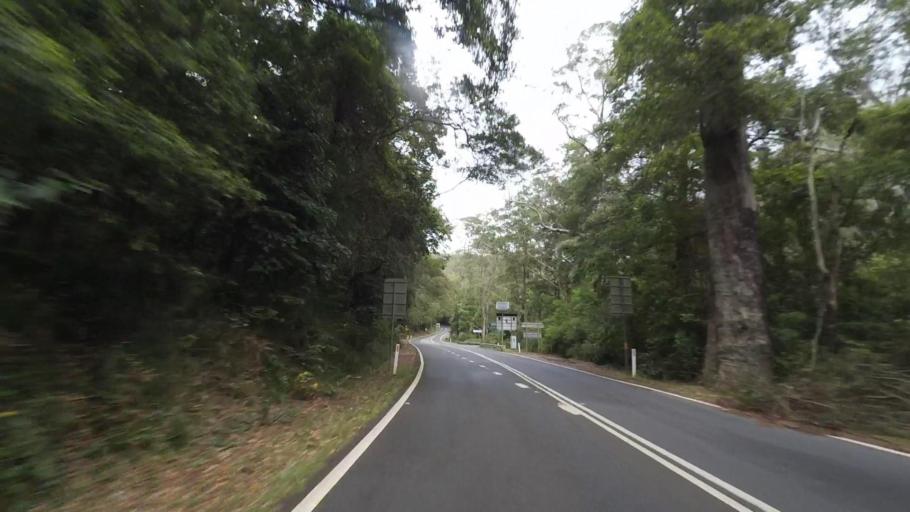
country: AU
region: New South Wales
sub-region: Wollongong
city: Helensburgh
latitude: -34.1515
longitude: 151.0288
